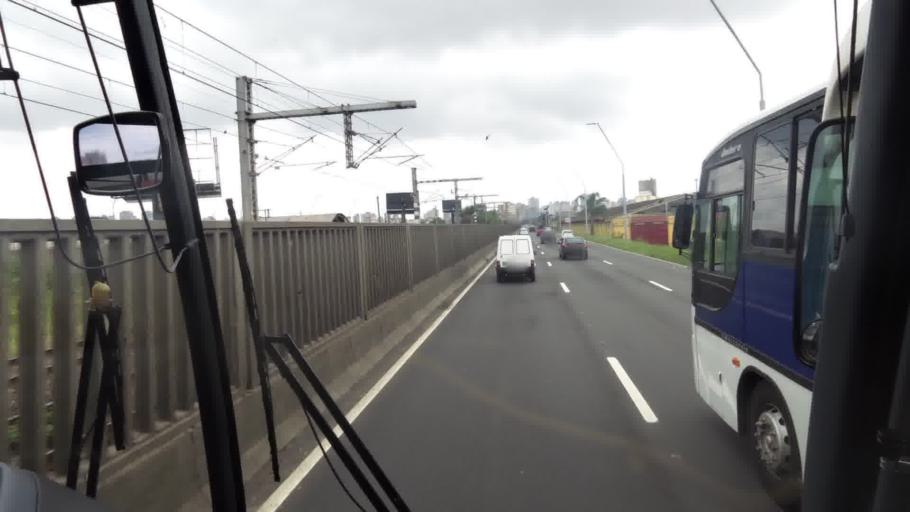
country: BR
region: Rio Grande do Sul
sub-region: Porto Alegre
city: Porto Alegre
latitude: -30.0126
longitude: -51.2128
